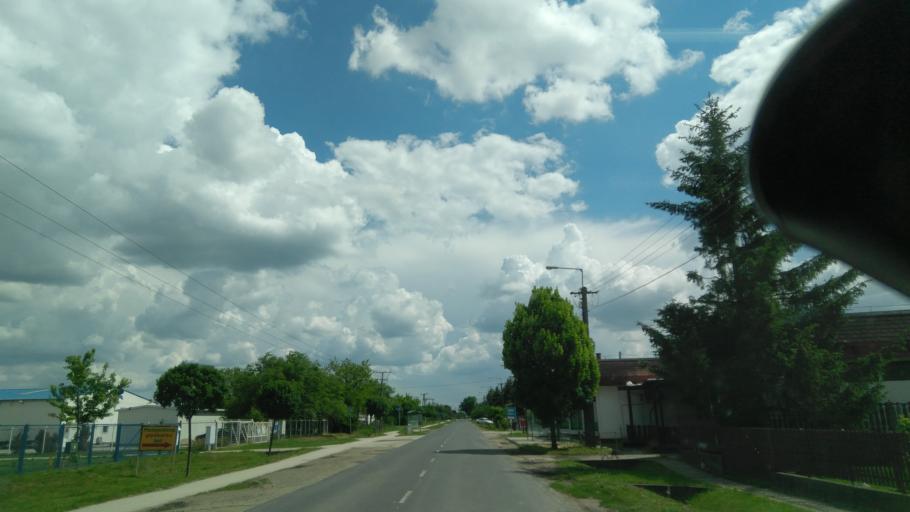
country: HU
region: Bekes
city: Devavanya
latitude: 47.0396
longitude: 20.9427
